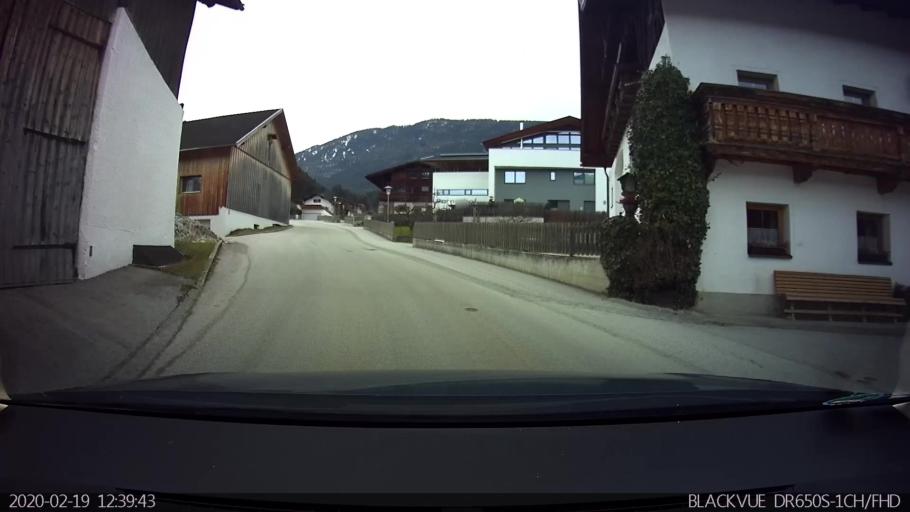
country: AT
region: Tyrol
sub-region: Politischer Bezirk Schwaz
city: Terfens
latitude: 47.3228
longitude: 11.6426
